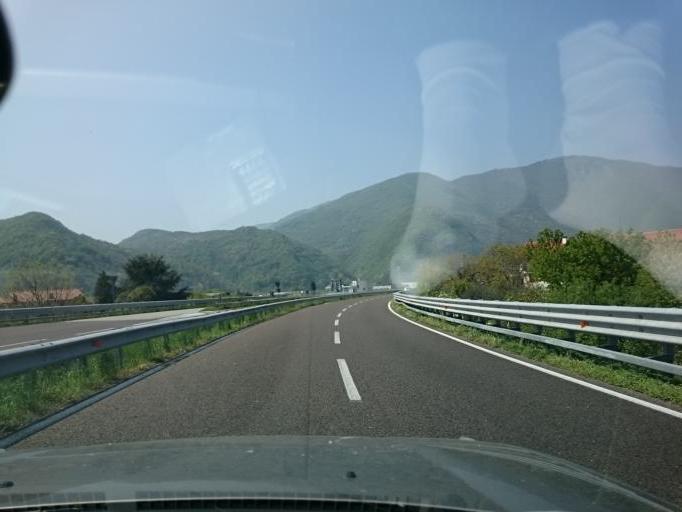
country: IT
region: Veneto
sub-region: Provincia di Vicenza
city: Pove del Grappa
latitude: 45.7882
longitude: 11.7312
